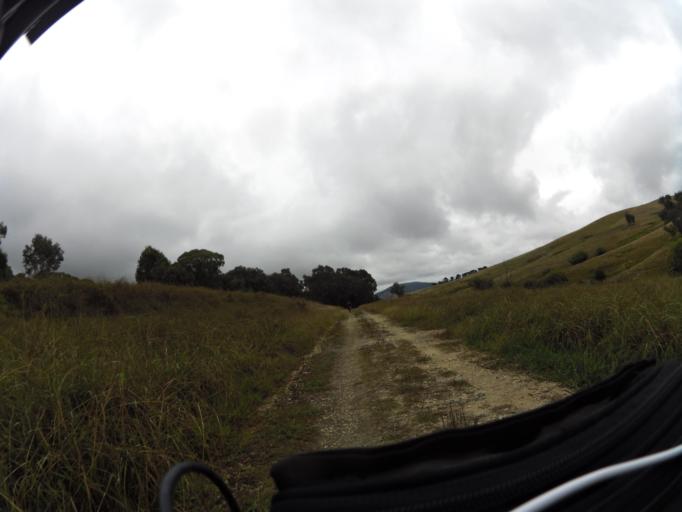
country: AU
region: New South Wales
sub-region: Greater Hume Shire
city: Holbrook
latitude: -36.1607
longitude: 147.4091
